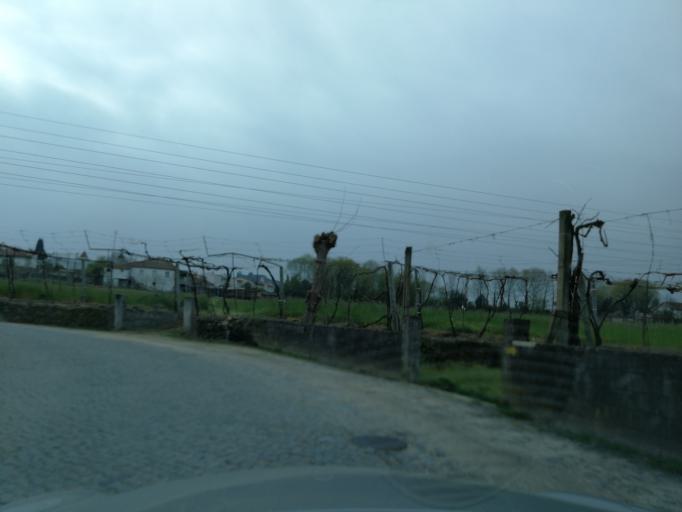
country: PT
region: Braga
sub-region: Braga
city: Braga
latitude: 41.5695
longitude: -8.4414
